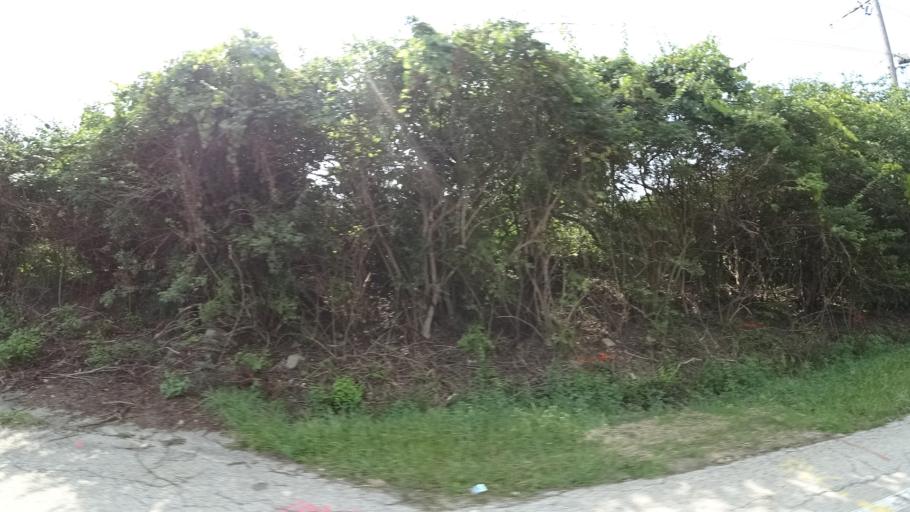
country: US
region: Illinois
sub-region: Will County
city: Goodings Grove
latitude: 41.6625
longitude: -87.8932
